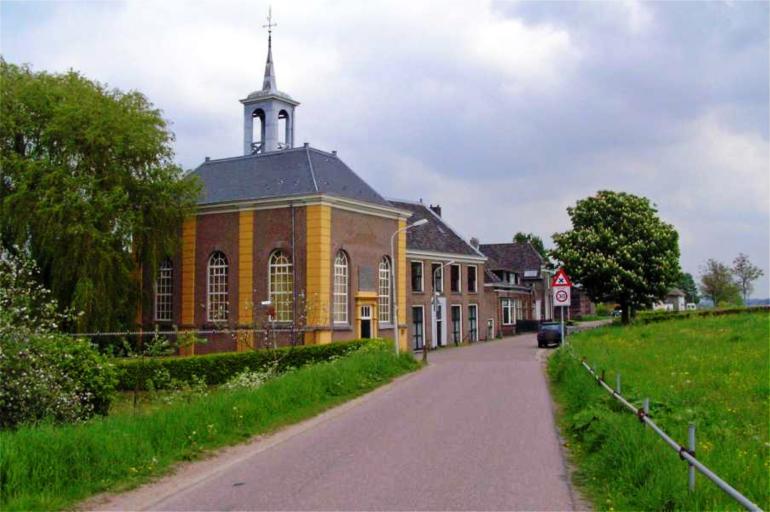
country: NL
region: Friesland
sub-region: Gemeente Franekeradeel
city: Tzum
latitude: 53.1587
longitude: 5.5632
